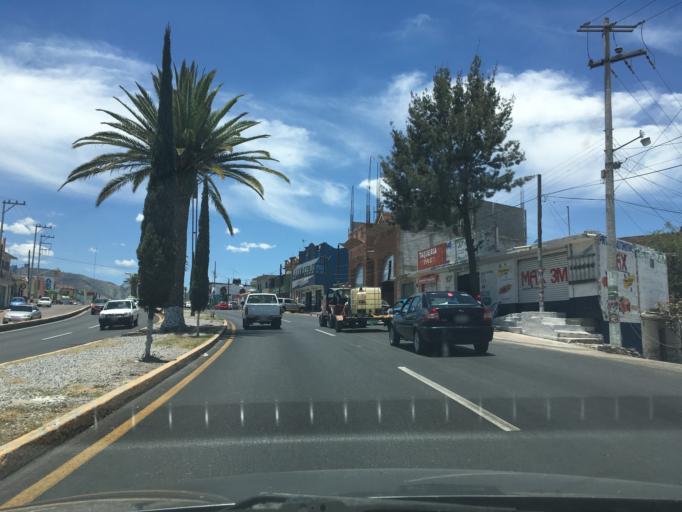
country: MX
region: Hidalgo
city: Actopan
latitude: 20.2633
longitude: -98.9462
